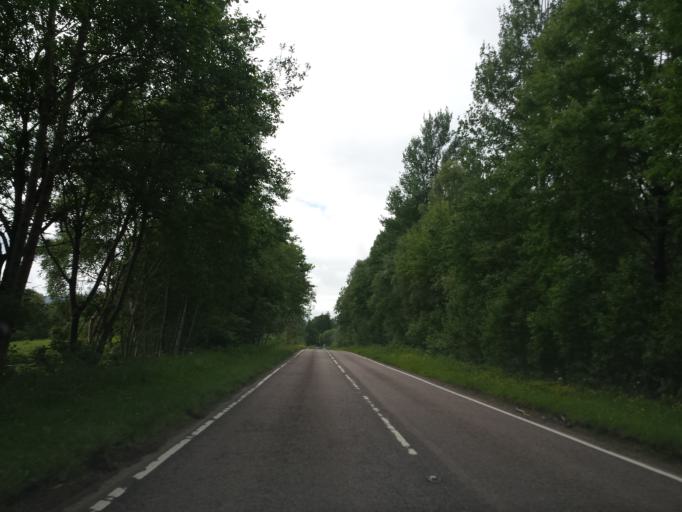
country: GB
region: Scotland
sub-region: Highland
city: Fort William
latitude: 56.8550
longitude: -5.2508
